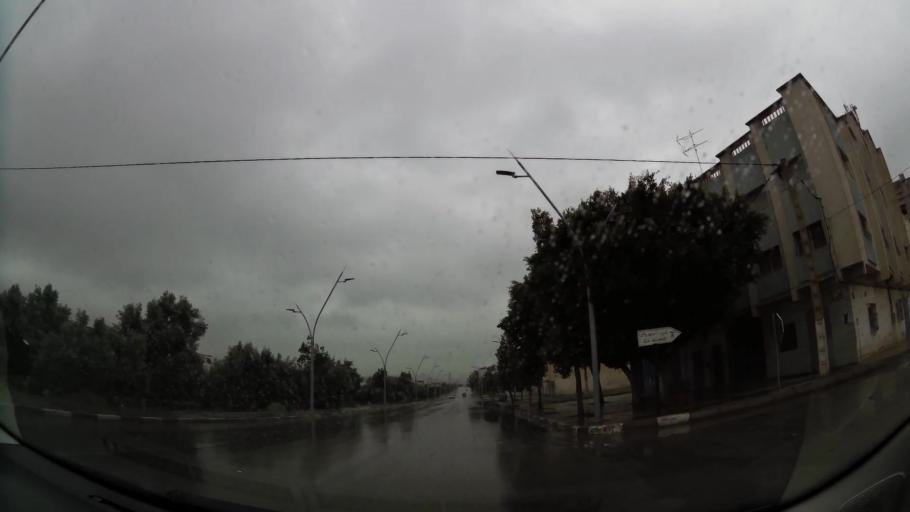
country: MA
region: Oriental
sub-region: Nador
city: Nador
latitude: 35.1585
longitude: -2.9714
